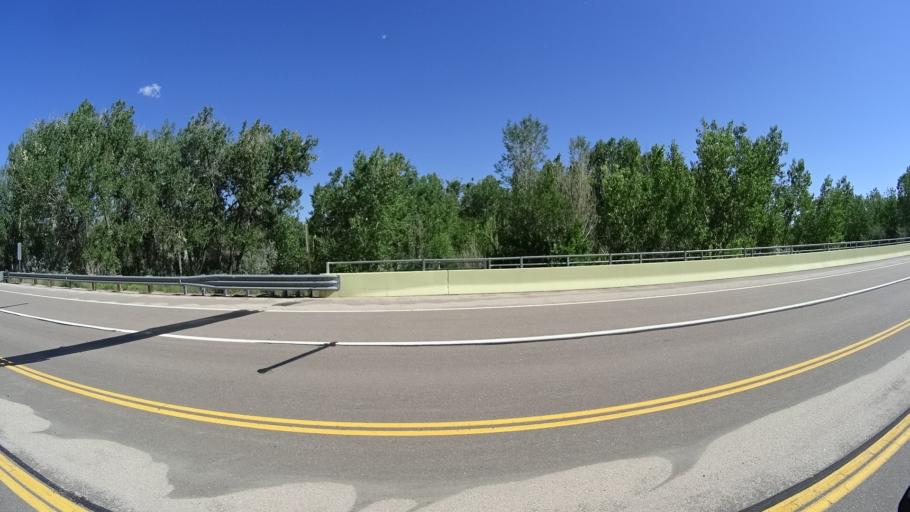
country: US
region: Colorado
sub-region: El Paso County
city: Security-Widefield
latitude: 38.7621
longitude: -104.6534
